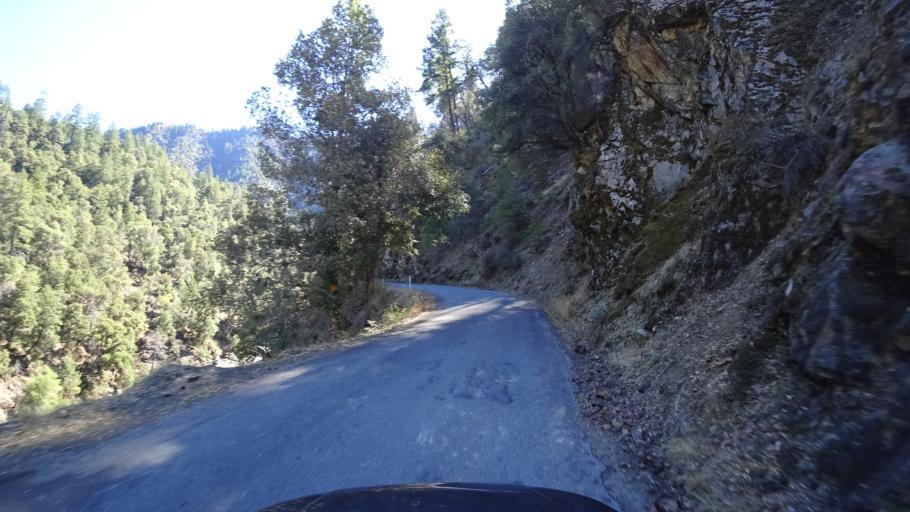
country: US
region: California
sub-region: Siskiyou County
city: Happy Camp
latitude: 41.3396
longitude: -123.3983
